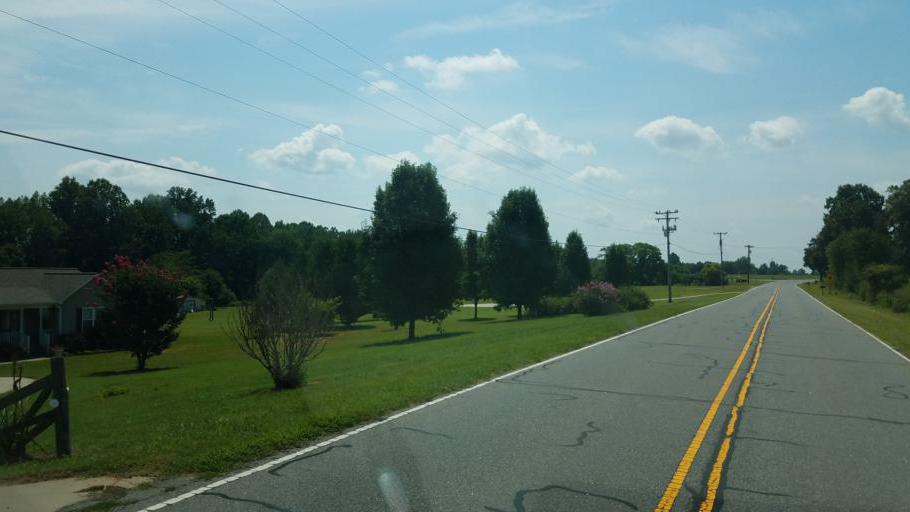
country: US
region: North Carolina
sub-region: Gaston County
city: Cherryville
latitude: 35.4657
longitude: -81.4368
